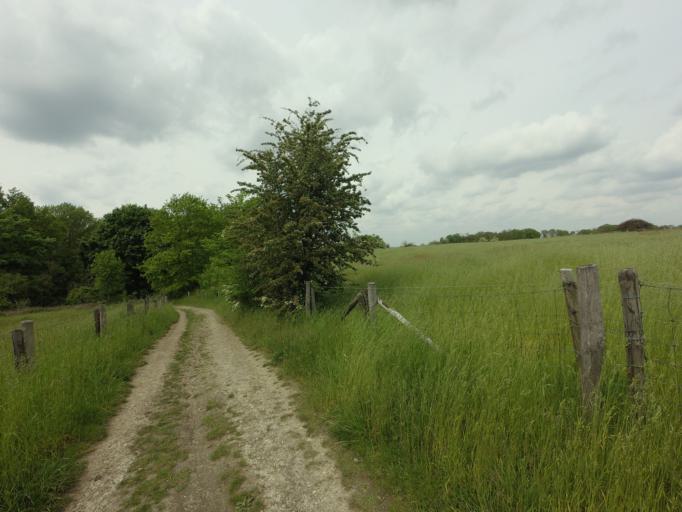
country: NL
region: Limburg
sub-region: Gemeente Maastricht
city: Heer
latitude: 50.8306
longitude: 5.7490
